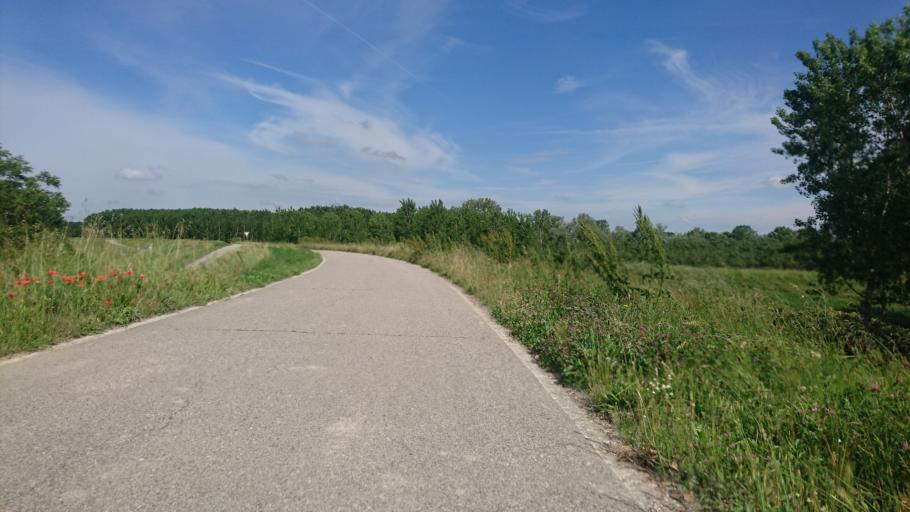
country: IT
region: Lombardy
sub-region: Provincia di Mantova
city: Borgofranco sul Po
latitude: 45.0520
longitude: 11.2075
